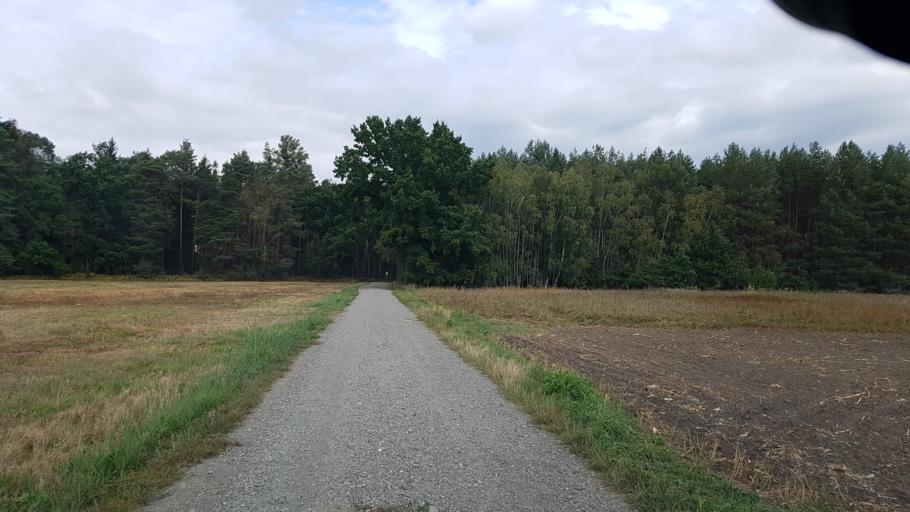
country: DE
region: Brandenburg
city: Ruckersdorf
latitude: 51.5669
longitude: 13.6435
